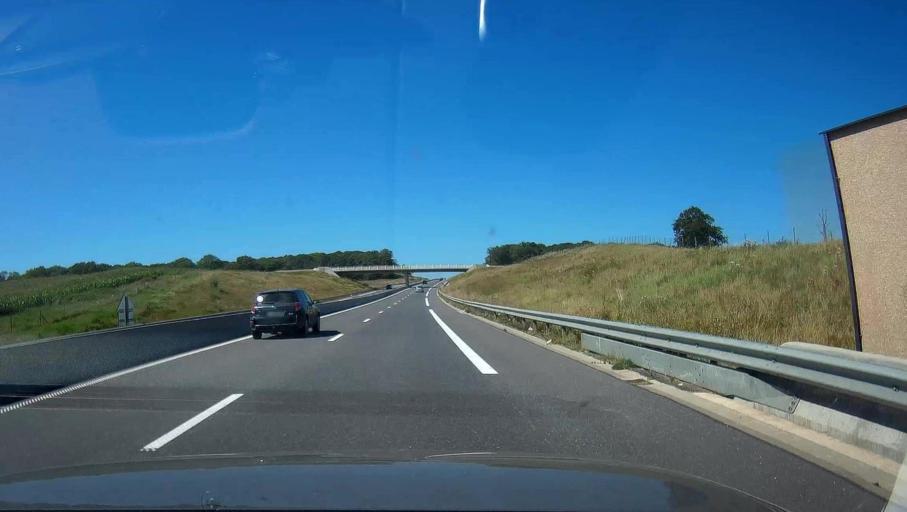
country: FR
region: Champagne-Ardenne
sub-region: Departement des Ardennes
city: Prix-les-Mezieres
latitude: 49.7516
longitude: 4.6609
